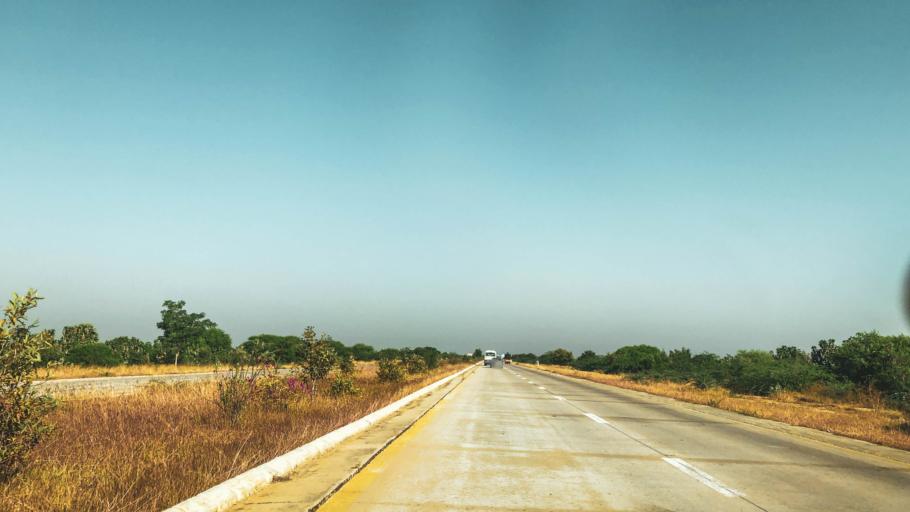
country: MM
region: Sagain
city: Sagaing
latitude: 21.7862
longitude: 95.9688
